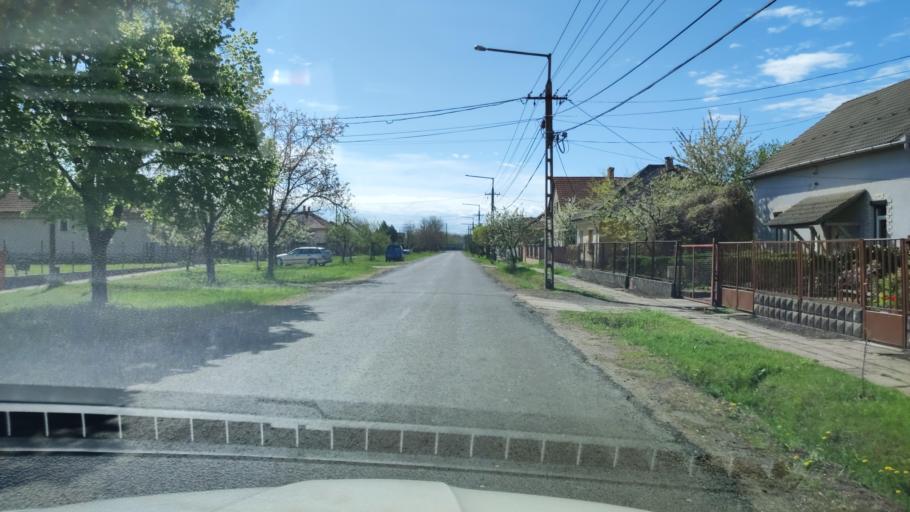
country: HU
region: Pest
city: Abony
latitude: 47.1763
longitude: 20.0145
